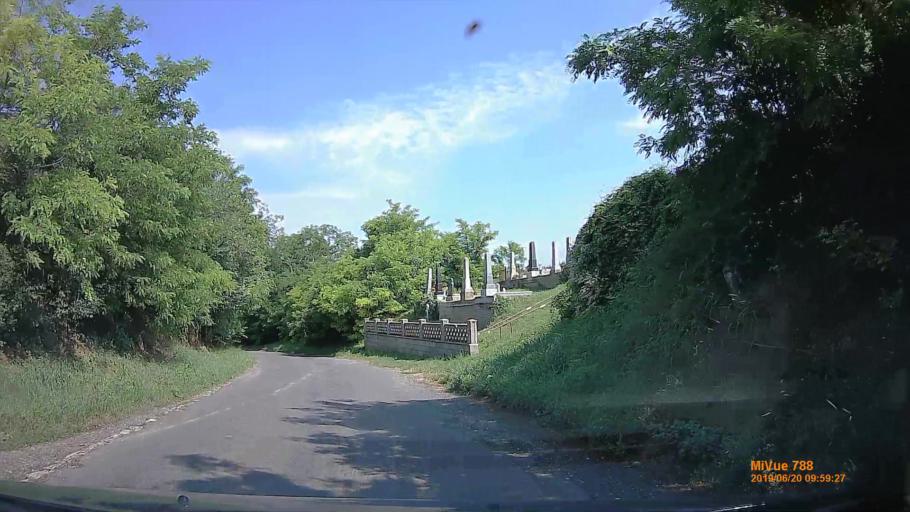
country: HU
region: Baranya
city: Pecsvarad
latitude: 46.1648
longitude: 18.4365
